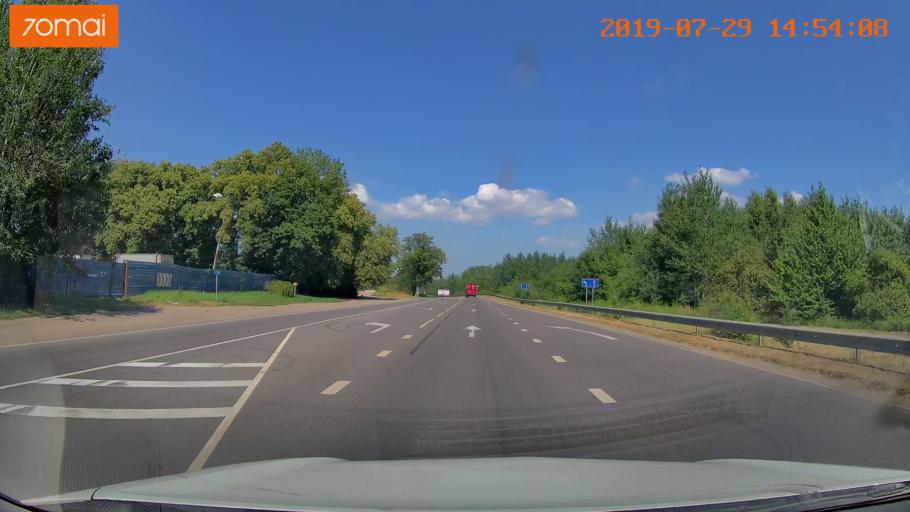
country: RU
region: Kaliningrad
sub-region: Gorod Kaliningrad
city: Baltiysk
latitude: 54.6713
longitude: 19.9226
